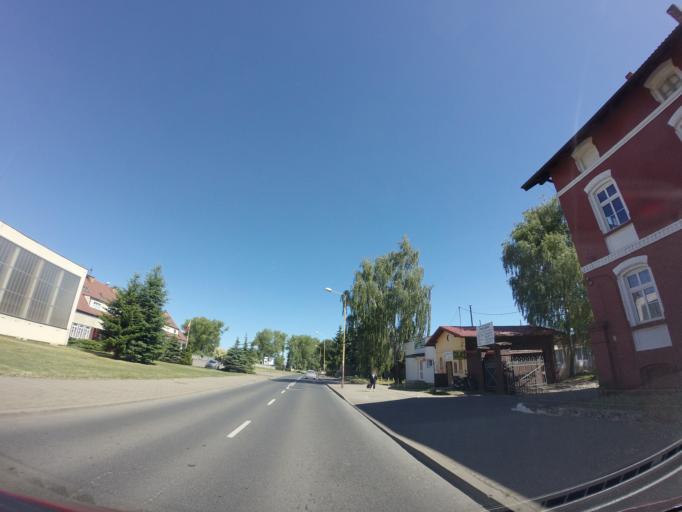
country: PL
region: West Pomeranian Voivodeship
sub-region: Powiat pyrzycki
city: Pyrzyce
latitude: 53.1500
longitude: 14.8926
